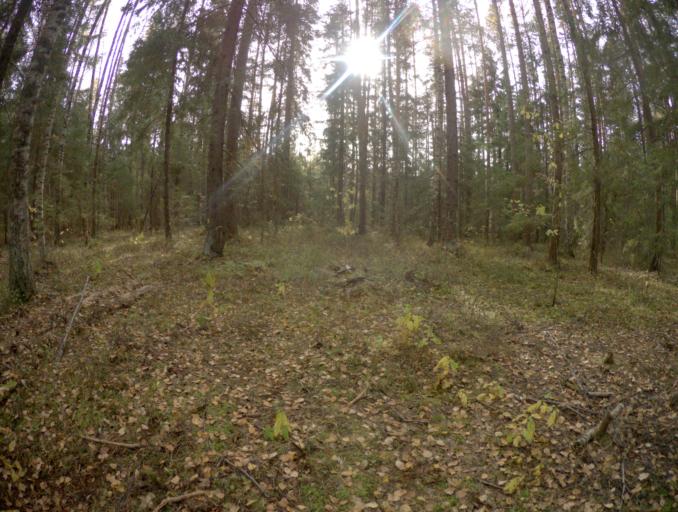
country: RU
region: Vladimir
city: Vorsha
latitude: 55.9614
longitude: 40.1417
